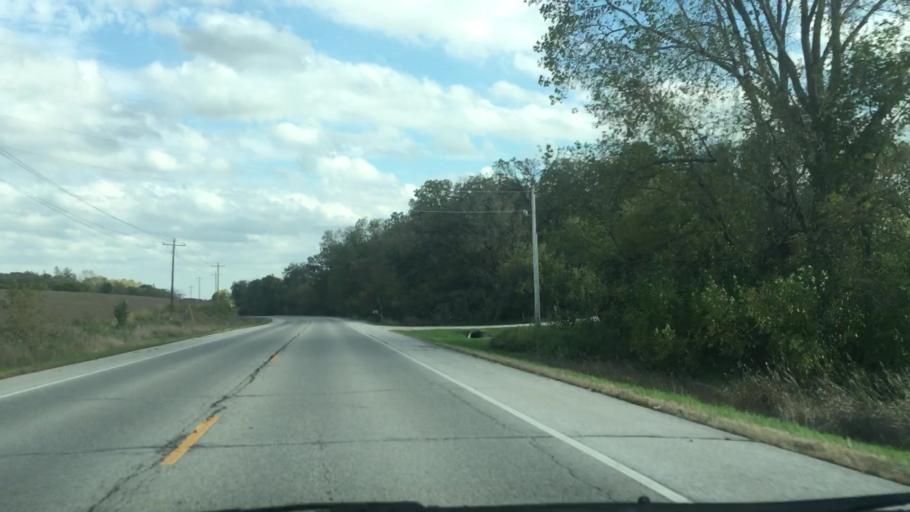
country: US
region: Minnesota
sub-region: Olmsted County
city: Eyota
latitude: 43.9110
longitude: -92.2658
